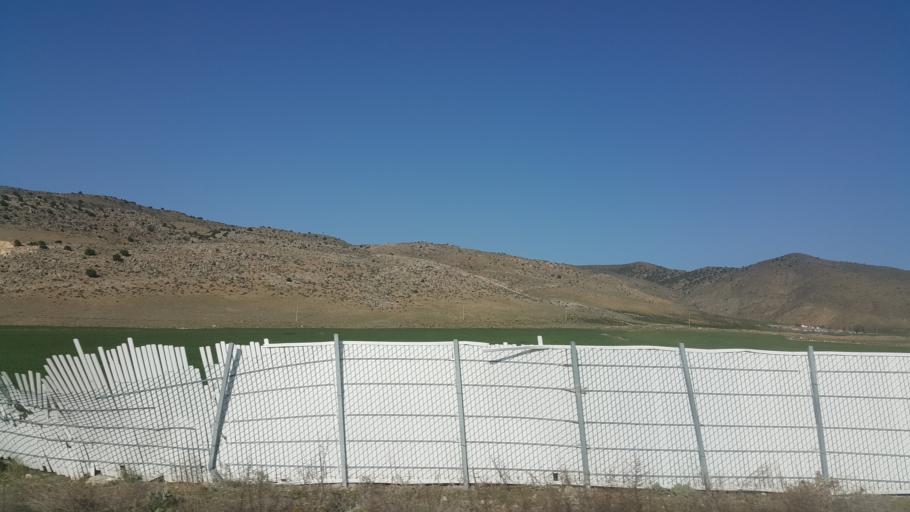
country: TR
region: Ankara
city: Sereflikochisar
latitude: 38.7613
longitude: 33.6559
